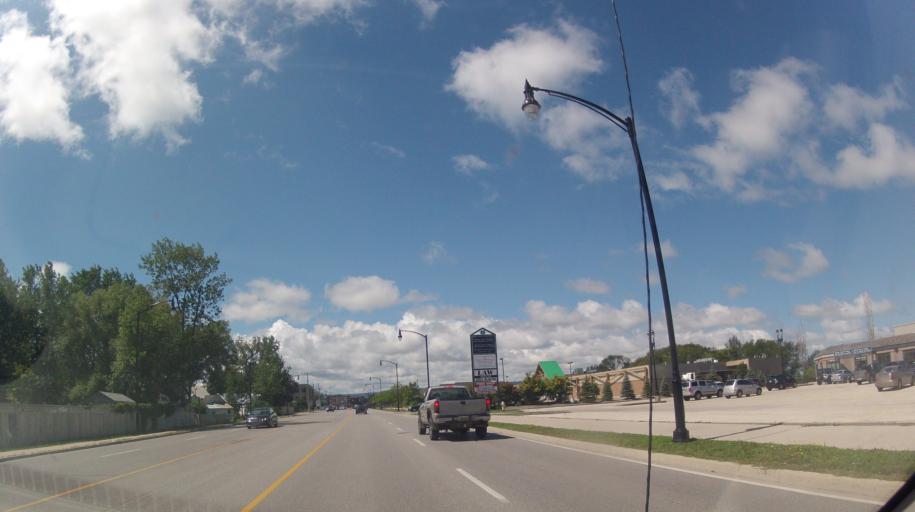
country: CA
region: Ontario
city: Collingwood
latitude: 44.5051
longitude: -80.2110
